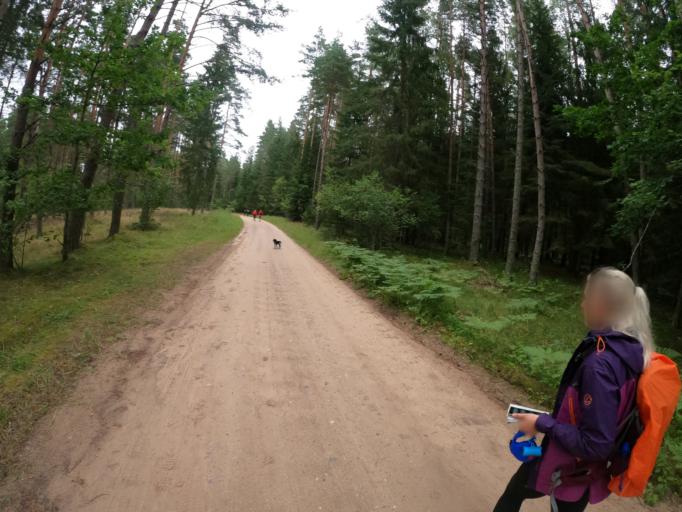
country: LV
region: Kuldigas Rajons
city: Kuldiga
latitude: 57.0143
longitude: 21.9866
